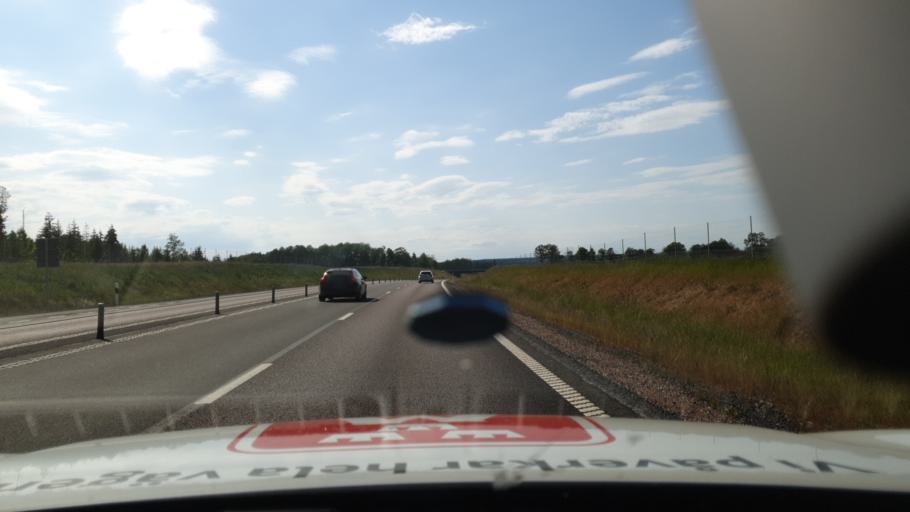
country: SE
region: Joenkoeping
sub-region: Habo Kommun
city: Habo
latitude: 57.8575
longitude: 14.0099
